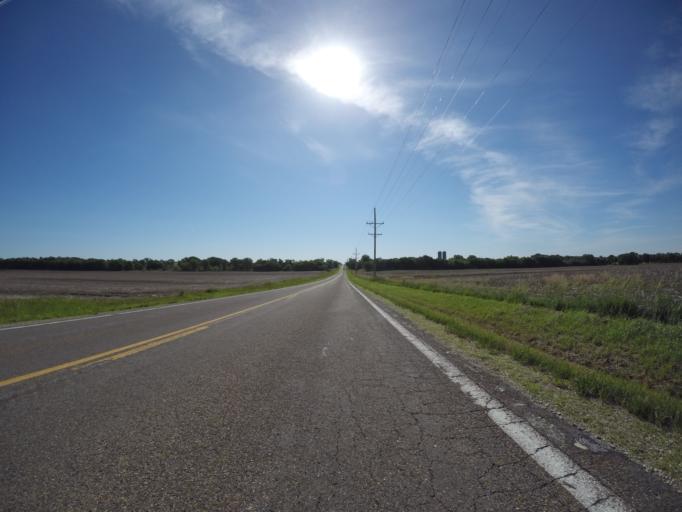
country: US
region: Kansas
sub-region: Mitchell County
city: Beloit
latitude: 39.6393
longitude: -97.9492
